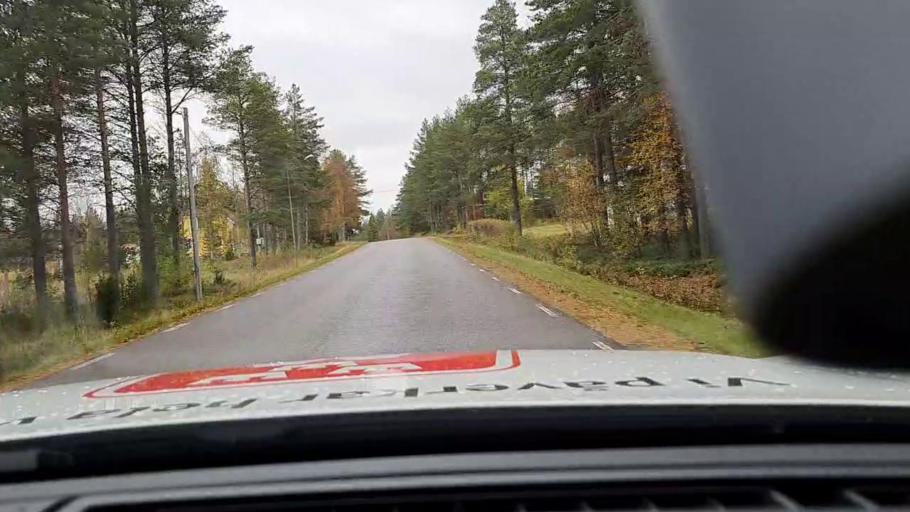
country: SE
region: Norrbotten
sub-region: Haparanda Kommun
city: Haparanda
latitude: 65.7837
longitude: 23.9200
